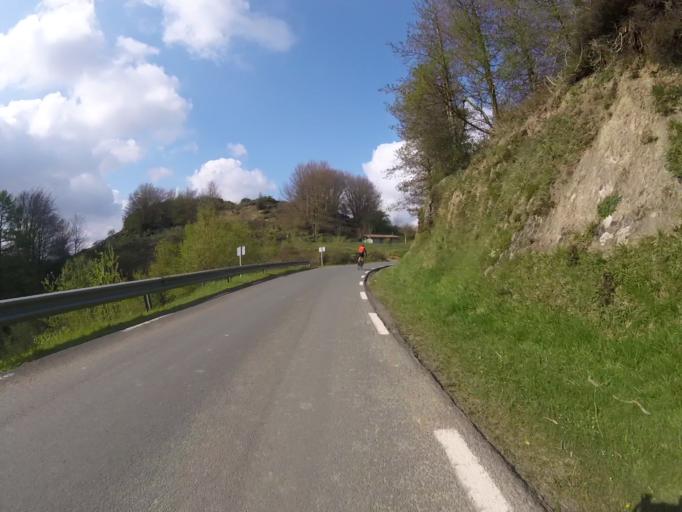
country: ES
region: Basque Country
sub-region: Provincia de Guipuzcoa
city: Azkoitia
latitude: 43.2090
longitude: -2.3263
